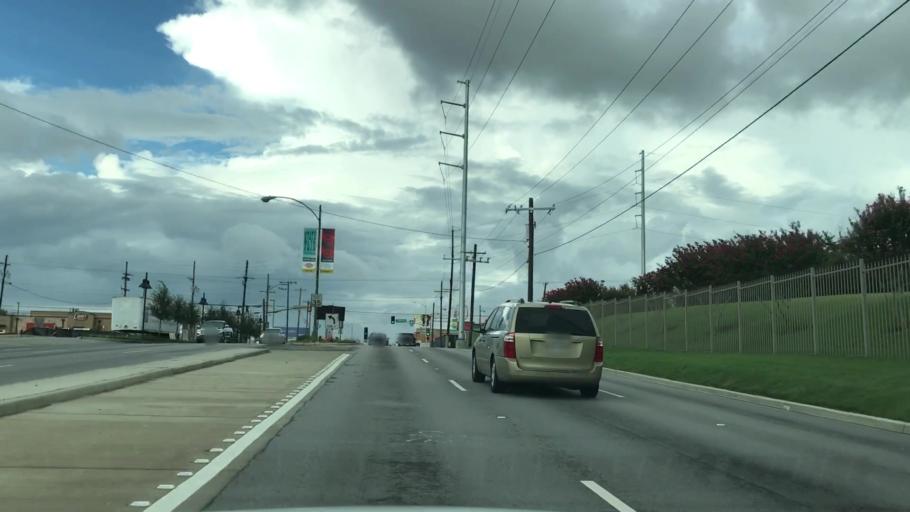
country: US
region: Texas
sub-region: Dallas County
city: University Park
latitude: 32.8271
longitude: -96.8455
